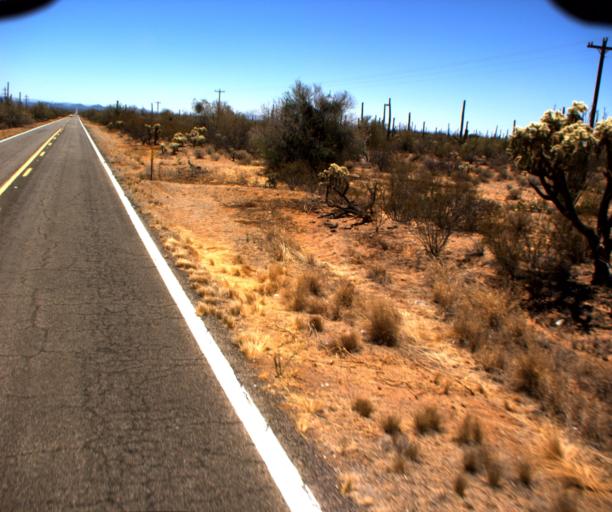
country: US
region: Arizona
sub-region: Pima County
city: Sells
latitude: 32.1337
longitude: -112.0926
